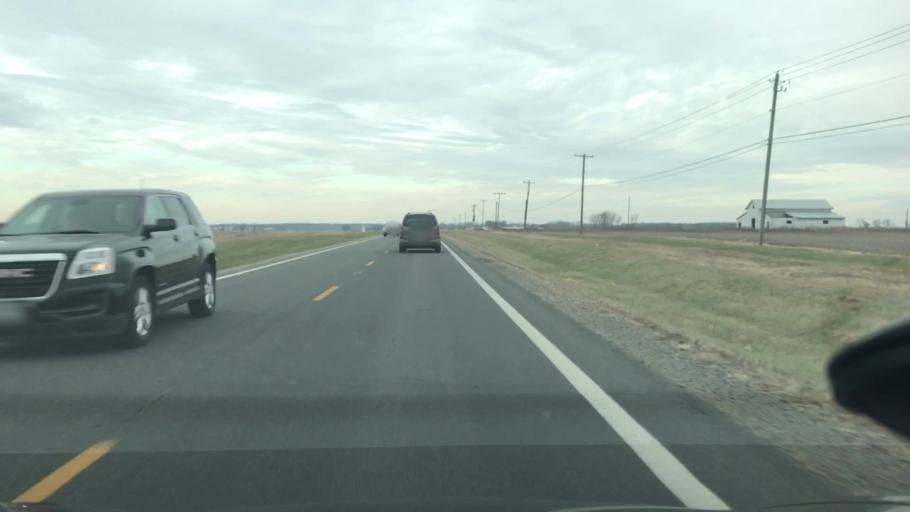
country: US
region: Ohio
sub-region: Madison County
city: London
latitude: 39.9149
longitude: -83.4787
